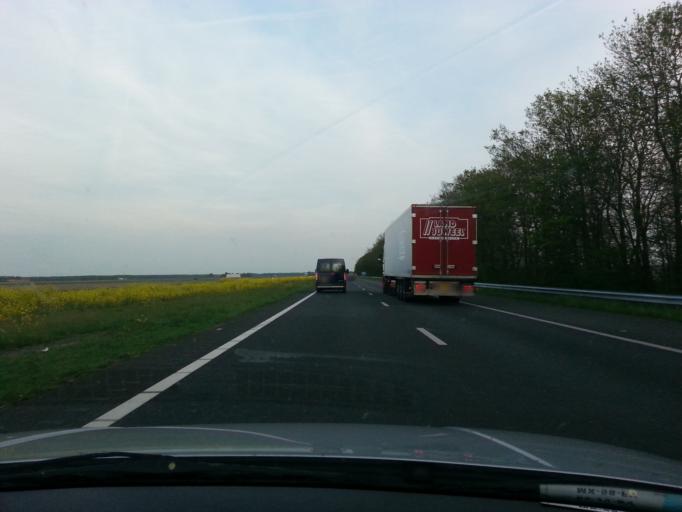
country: NL
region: Friesland
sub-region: Gemeente Lemsterland
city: Lemmer
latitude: 52.8319
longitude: 5.7313
